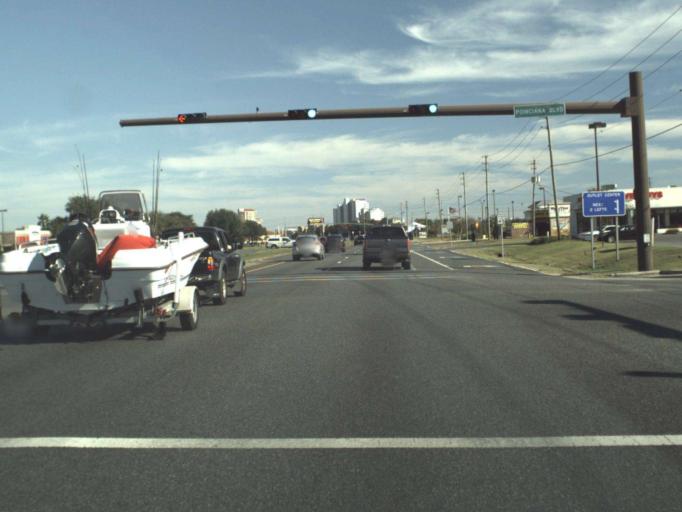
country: US
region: Florida
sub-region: Walton County
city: Miramar Beach
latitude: 30.3787
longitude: -86.3528
